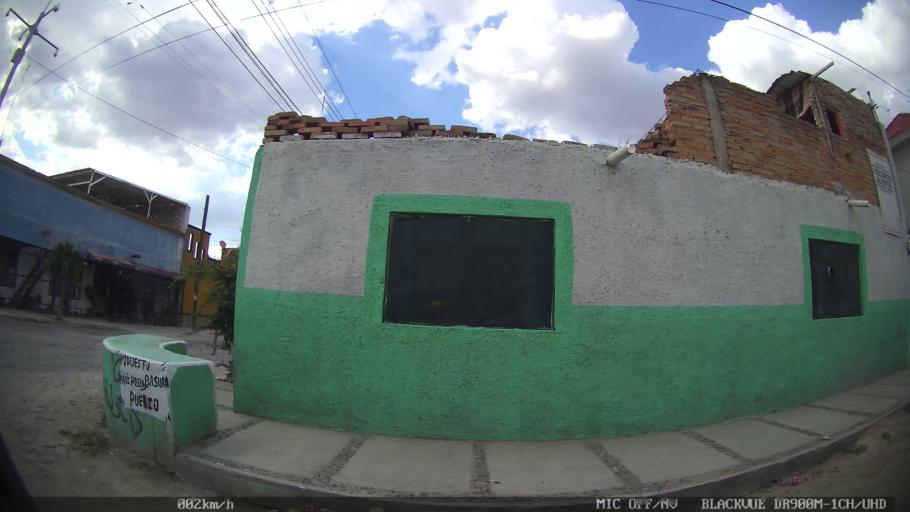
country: MX
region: Jalisco
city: Tlaquepaque
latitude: 20.6542
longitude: -103.2582
